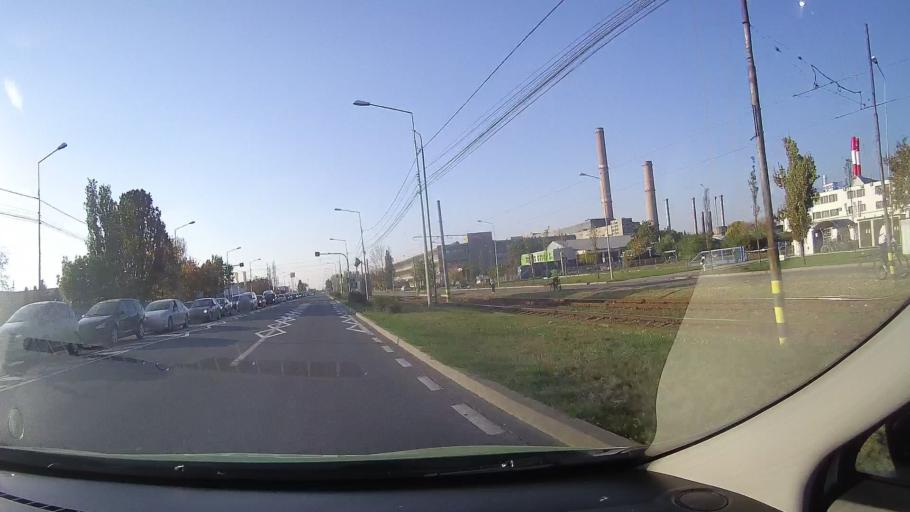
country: RO
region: Bihor
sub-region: Comuna Biharea
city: Oradea
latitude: 47.0793
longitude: 21.8963
